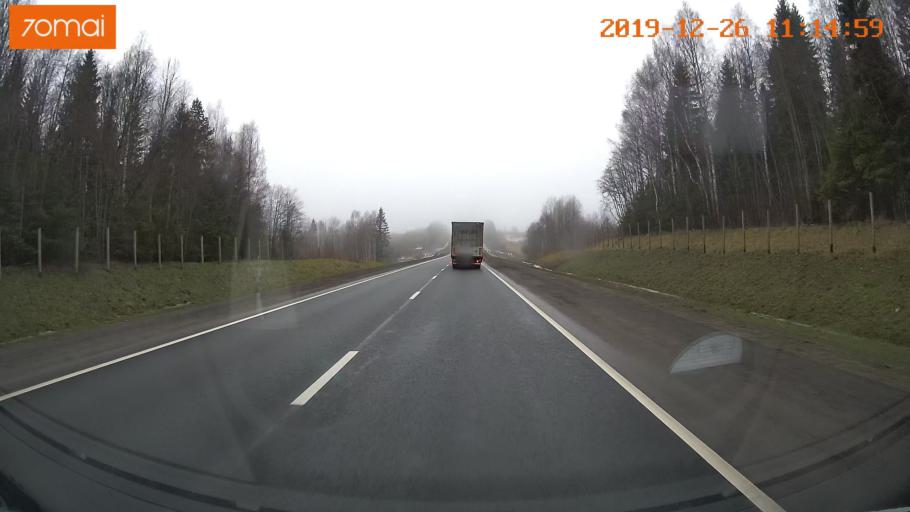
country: RU
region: Vologda
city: Chebsara
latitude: 59.1208
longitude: 39.1132
